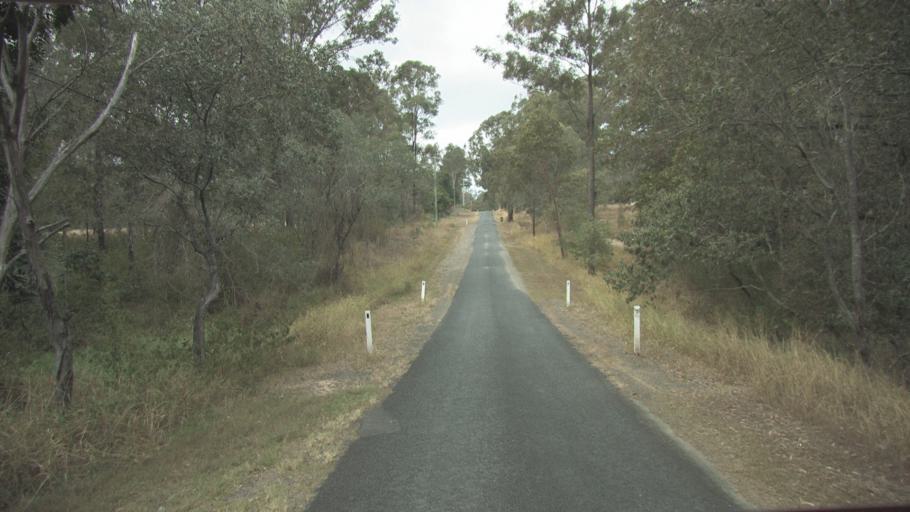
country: AU
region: Queensland
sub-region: Logan
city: Cedar Vale
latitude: -27.8826
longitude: 153.0292
